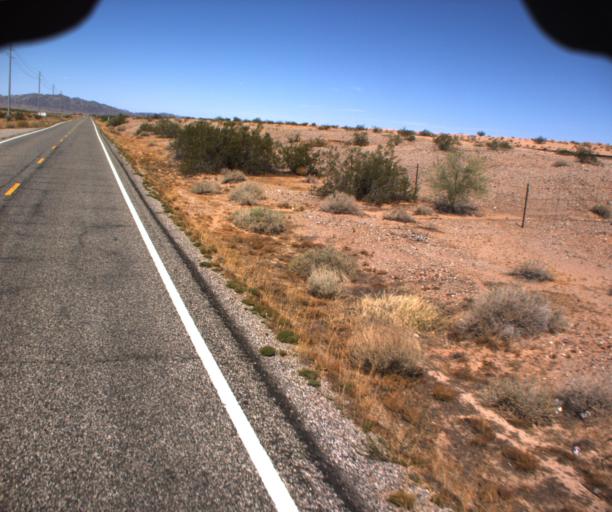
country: US
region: Arizona
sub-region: La Paz County
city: Cienega Springs
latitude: 33.9948
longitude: -114.1482
